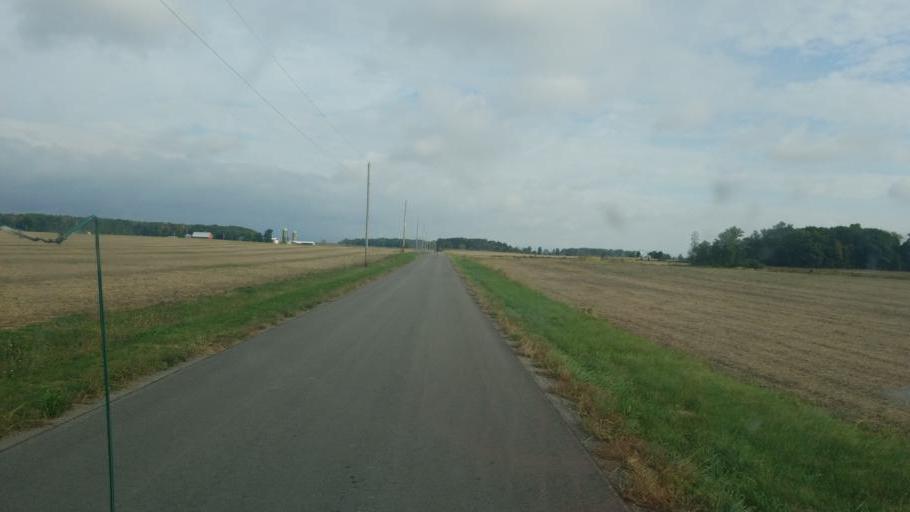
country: US
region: Ohio
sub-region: Wyandot County
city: Carey
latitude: 41.0241
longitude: -83.4487
